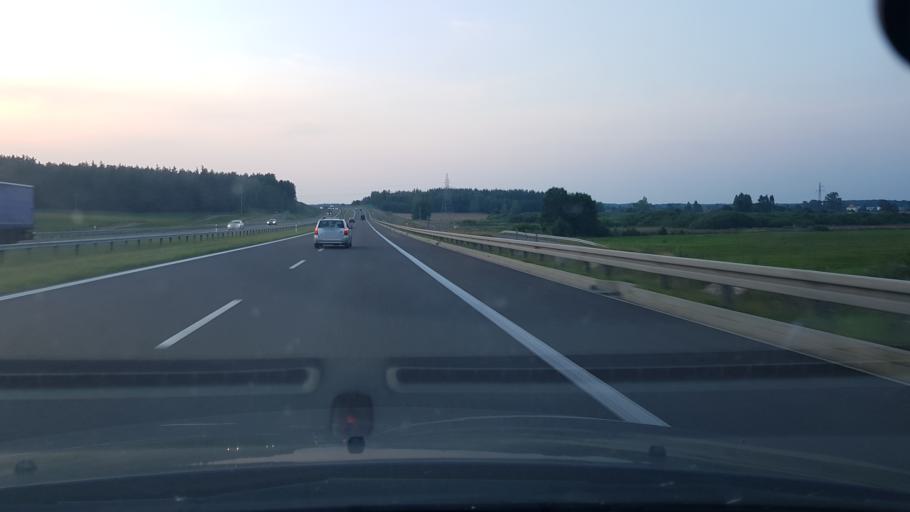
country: PL
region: Warmian-Masurian Voivodeship
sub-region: Powiat nidzicki
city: Nidzica
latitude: 53.3595
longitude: 20.3903
